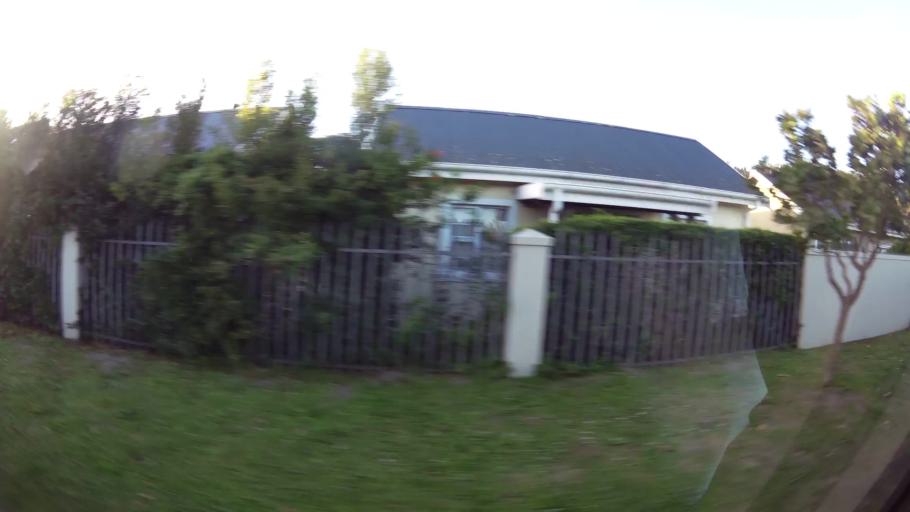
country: ZA
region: Western Cape
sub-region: Eden District Municipality
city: Knysna
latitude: -34.0127
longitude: 22.7940
